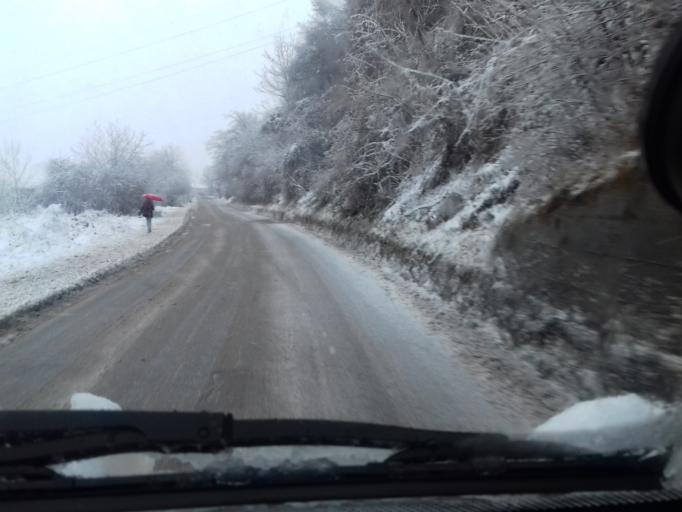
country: BA
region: Federation of Bosnia and Herzegovina
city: Zenica
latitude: 44.1843
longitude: 17.9504
